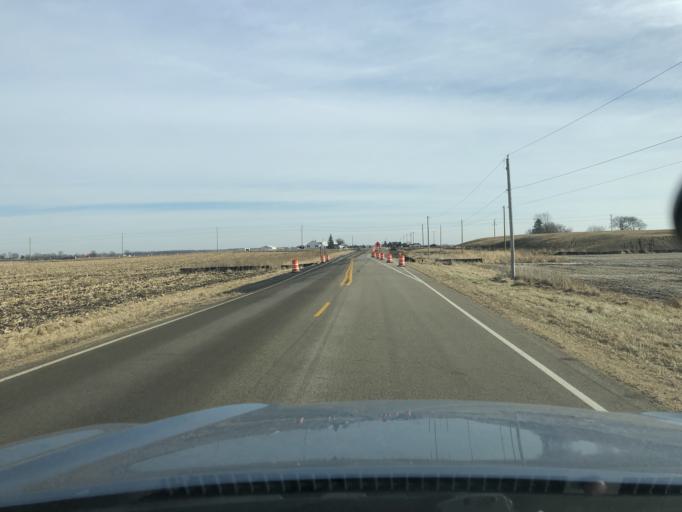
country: US
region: Illinois
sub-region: McHenry County
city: Marengo
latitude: 42.1824
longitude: -88.6222
